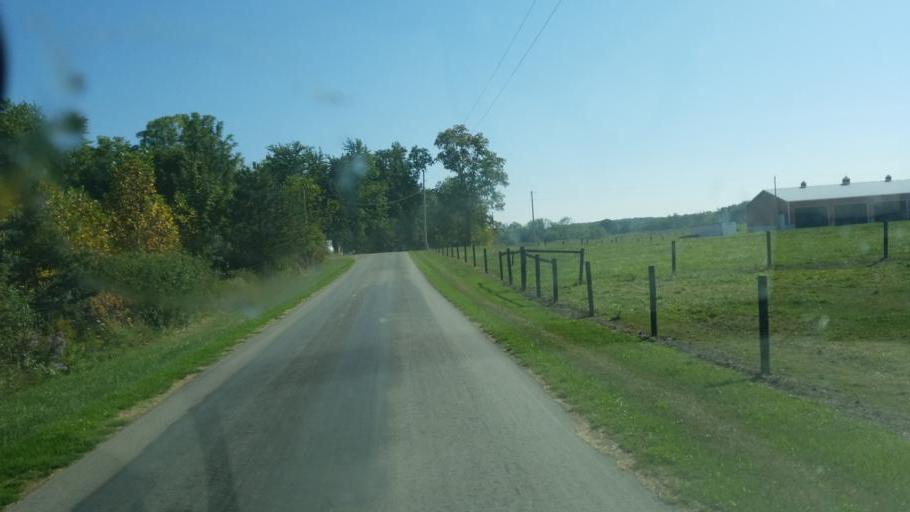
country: US
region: Ohio
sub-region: Union County
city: Richwood
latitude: 40.5549
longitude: -83.4193
